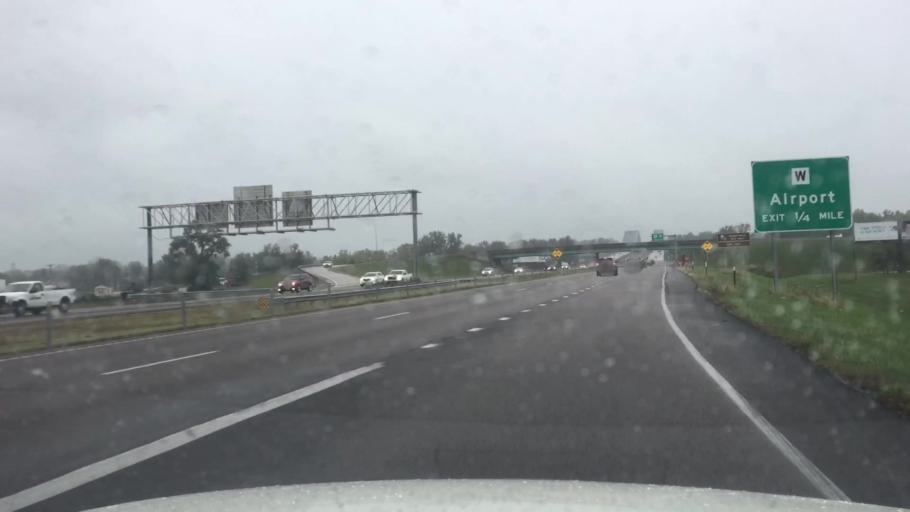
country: US
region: Missouri
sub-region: Cole County
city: Jefferson City
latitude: 38.5972
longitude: -92.1699
